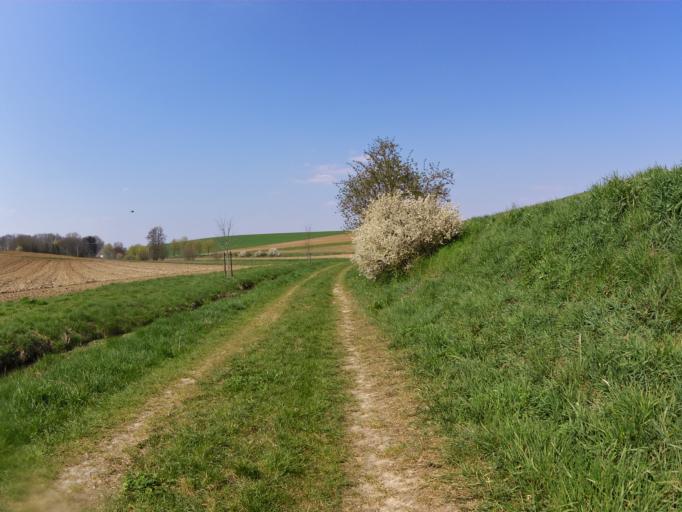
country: DE
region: Bavaria
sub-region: Regierungsbezirk Unterfranken
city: Dettelbach
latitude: 49.8198
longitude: 10.1467
